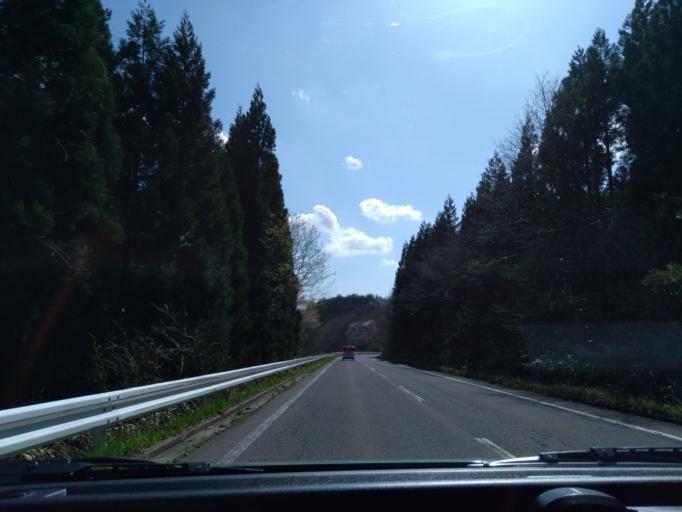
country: JP
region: Akita
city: Akita
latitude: 39.6945
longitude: 140.2484
